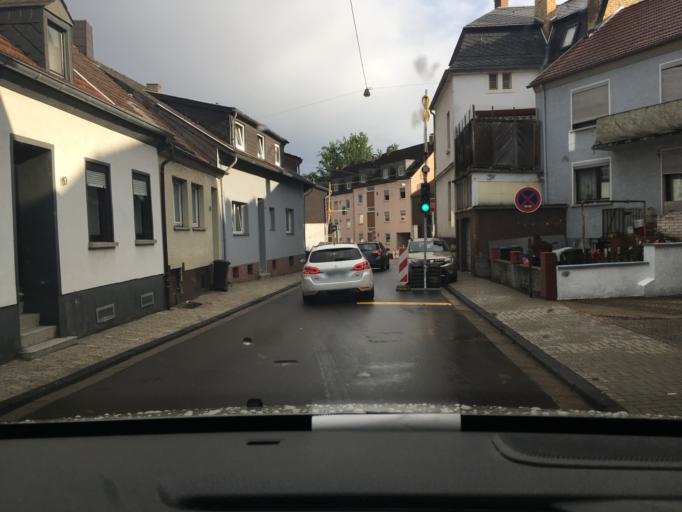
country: DE
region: Saarland
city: Sankt Ingbert
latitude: 49.2839
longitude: 7.1125
